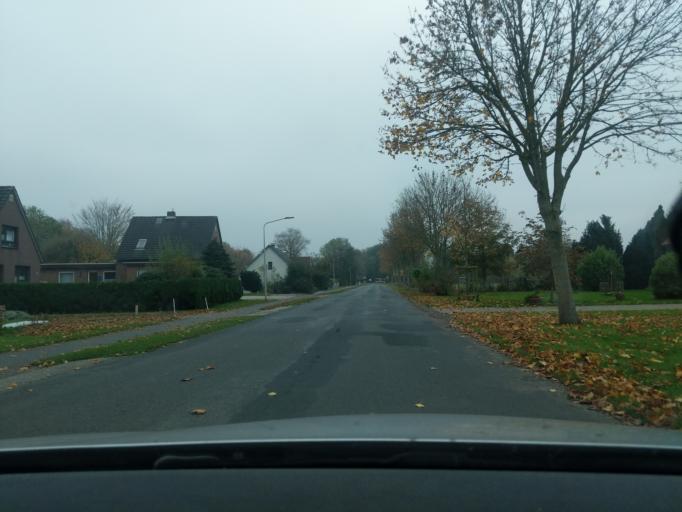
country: DE
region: Lower Saxony
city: Cuxhaven
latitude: 53.8344
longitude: 8.7346
